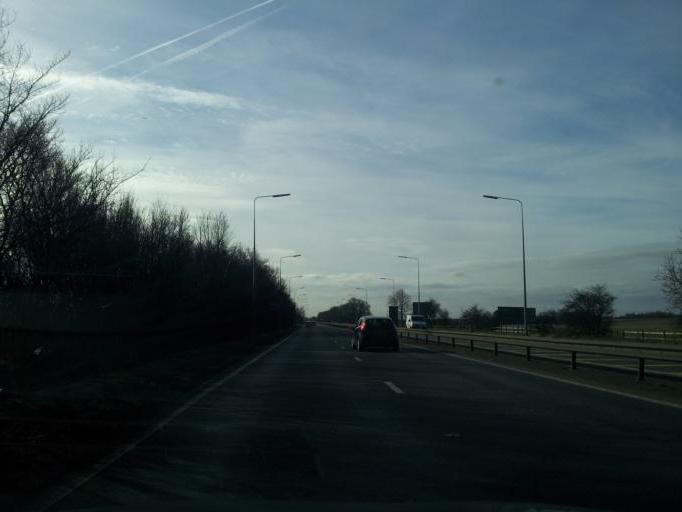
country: GB
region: England
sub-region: Central Bedfordshire
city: Biggleswade
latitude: 52.0914
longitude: -0.2741
